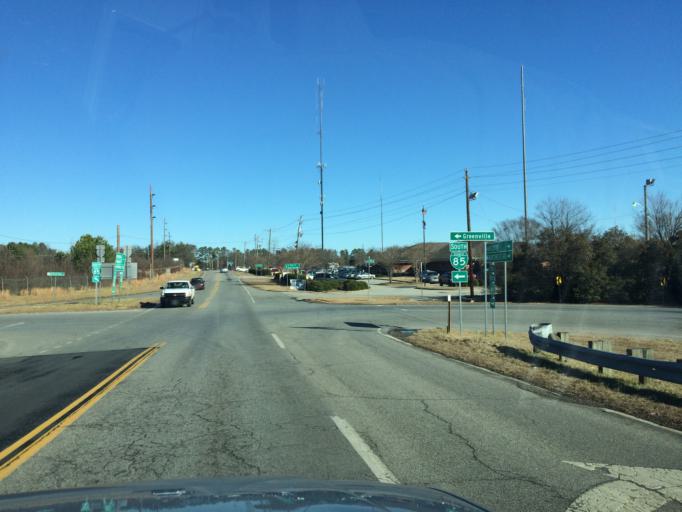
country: US
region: South Carolina
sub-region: Spartanburg County
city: Southern Shops
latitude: 34.9713
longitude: -81.9987
